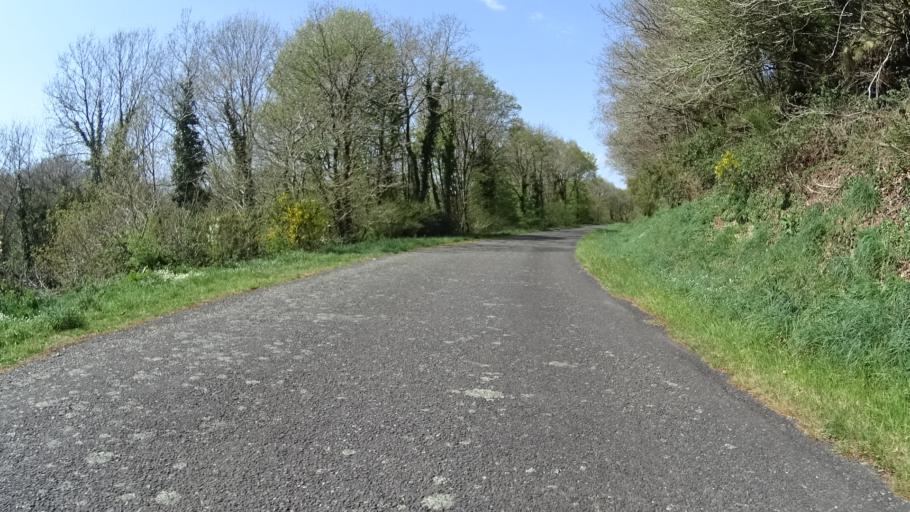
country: FR
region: Brittany
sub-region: Departement du Finistere
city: Sizun
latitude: 48.4171
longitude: -4.0968
